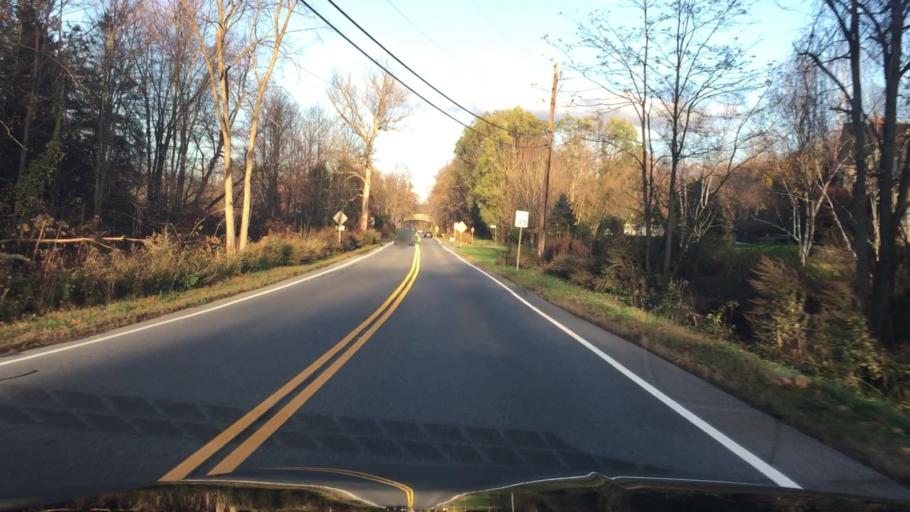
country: US
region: New York
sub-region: Dutchess County
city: Hillside Lake
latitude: 41.6427
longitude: -73.7913
